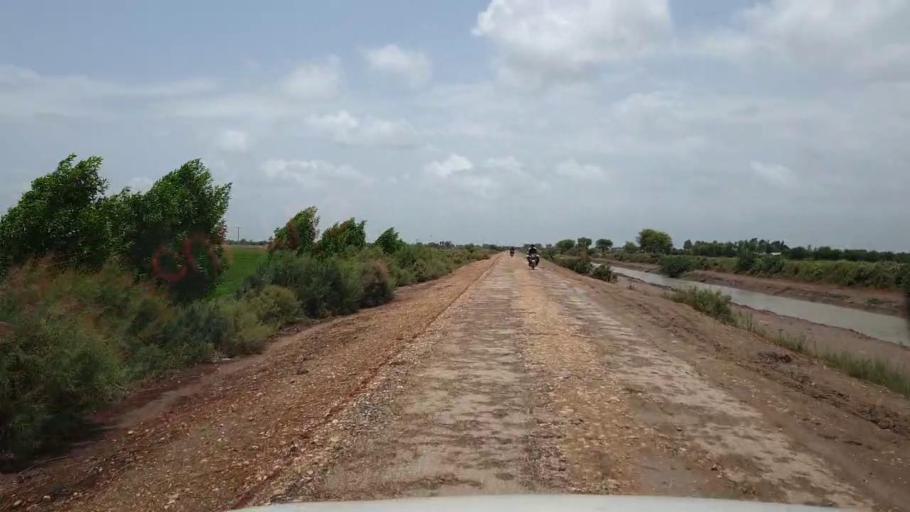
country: PK
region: Sindh
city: Kario
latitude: 24.7139
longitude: 68.5898
